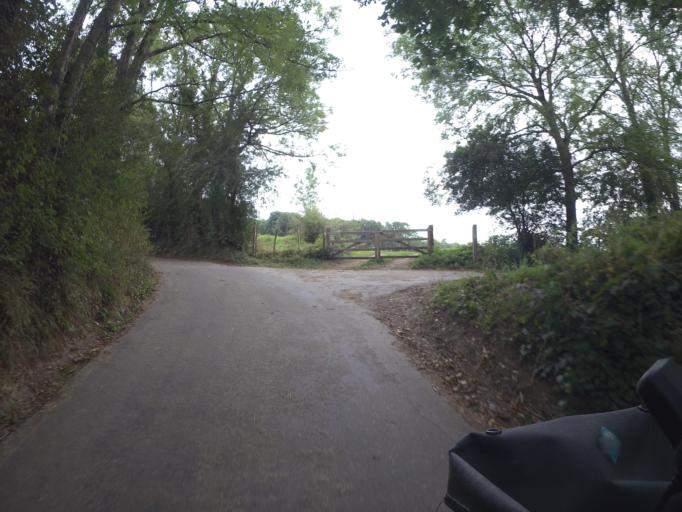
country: BE
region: Flanders
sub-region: Provincie Limburg
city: Sint-Pieters-Voeren
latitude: 50.7600
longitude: 5.7817
